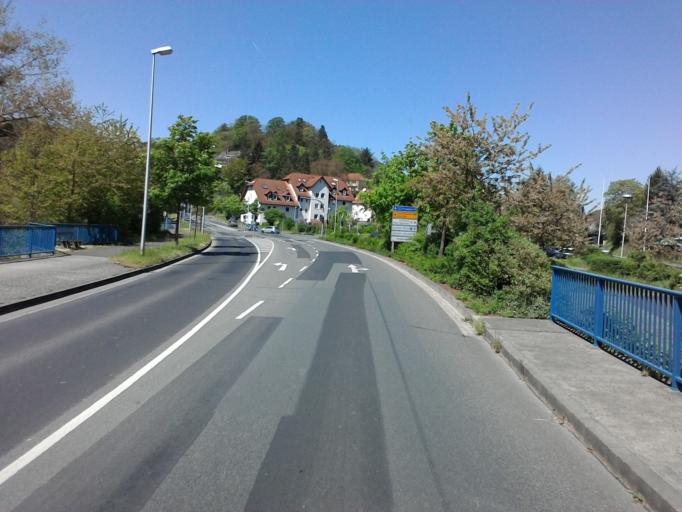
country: DE
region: Bavaria
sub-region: Regierungsbezirk Unterfranken
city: Lohr am Main
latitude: 49.9929
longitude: 9.5709
